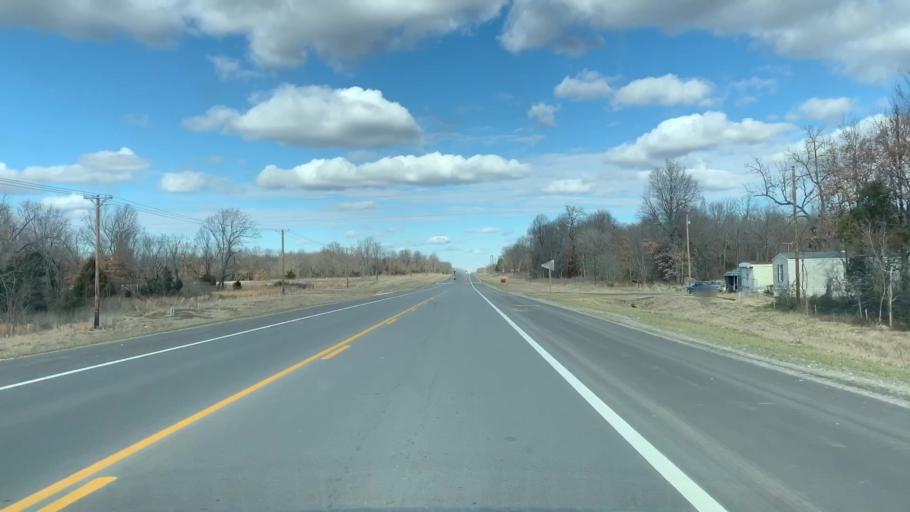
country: US
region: Kansas
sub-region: Cherokee County
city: Columbus
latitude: 37.2247
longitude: -94.8319
